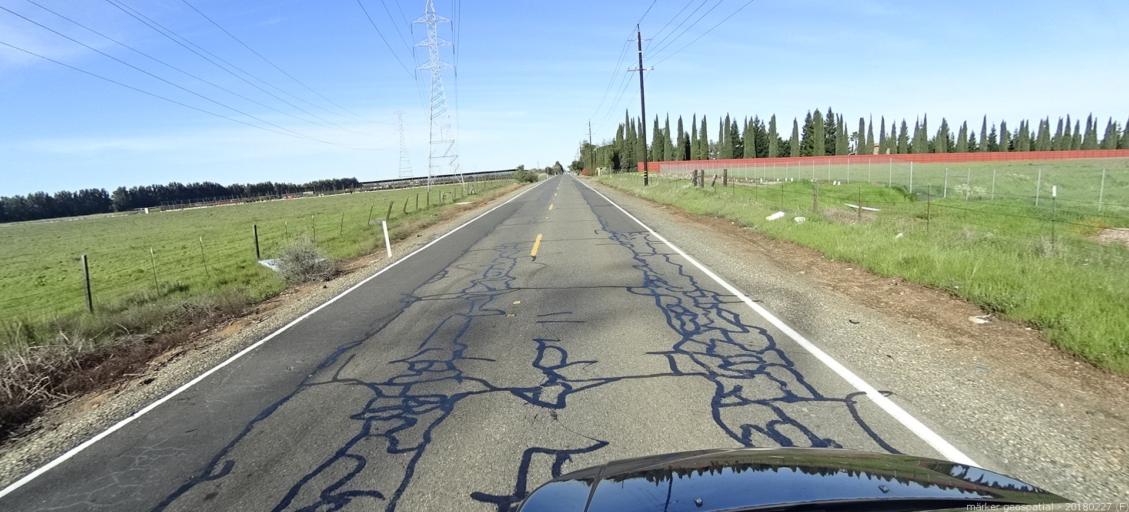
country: US
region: California
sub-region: Sacramento County
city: Vineyard
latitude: 38.5109
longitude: -121.3231
